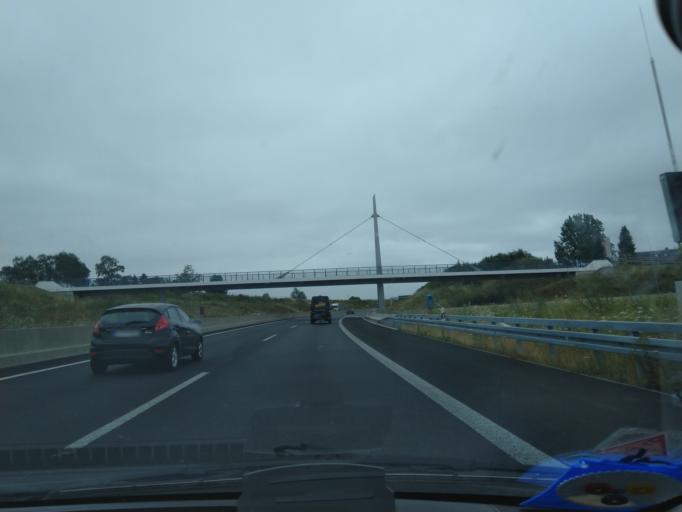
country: DE
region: North Rhine-Westphalia
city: Bad Oeynhausen
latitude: 52.2315
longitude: 8.8174
